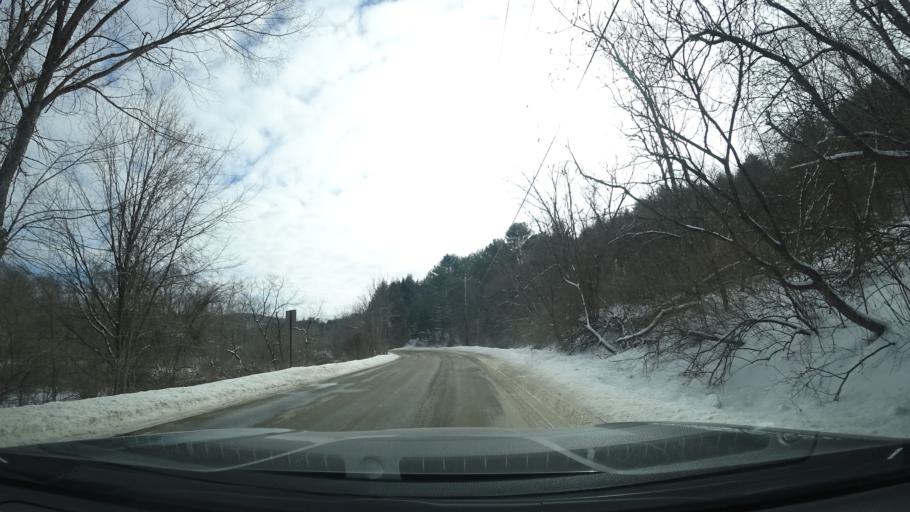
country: US
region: New York
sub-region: Washington County
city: Greenwich
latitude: 43.2276
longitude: -73.3633
